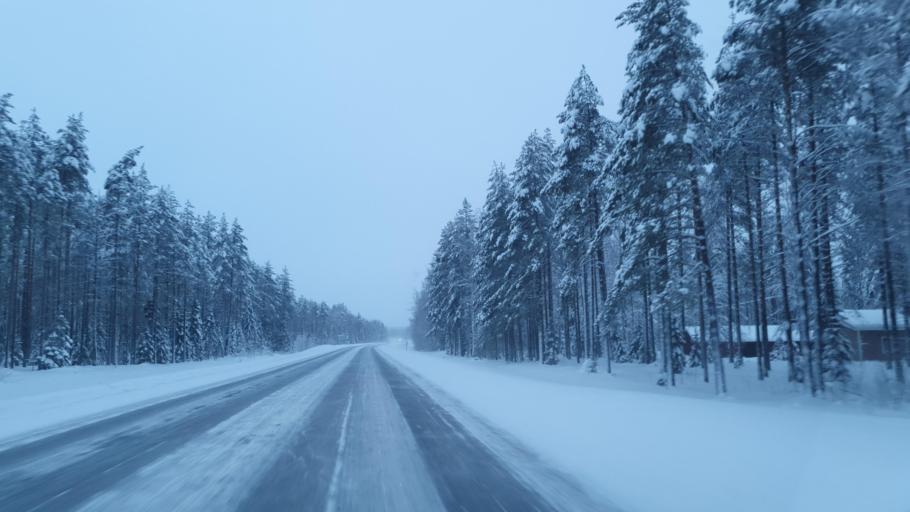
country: FI
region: Kainuu
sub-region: Kajaani
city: Vaala
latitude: 64.5544
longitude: 27.0430
